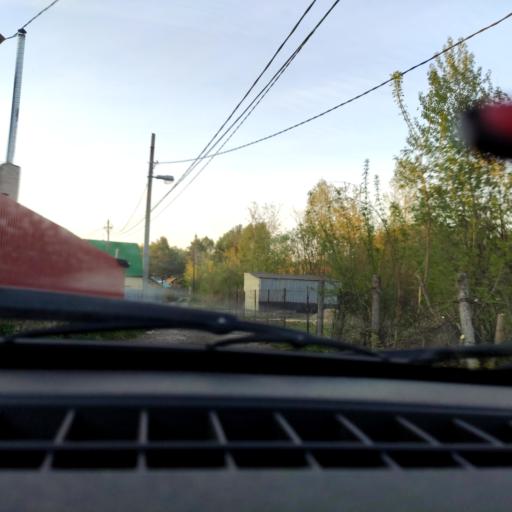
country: RU
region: Bashkortostan
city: Iglino
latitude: 54.8175
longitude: 56.1901
